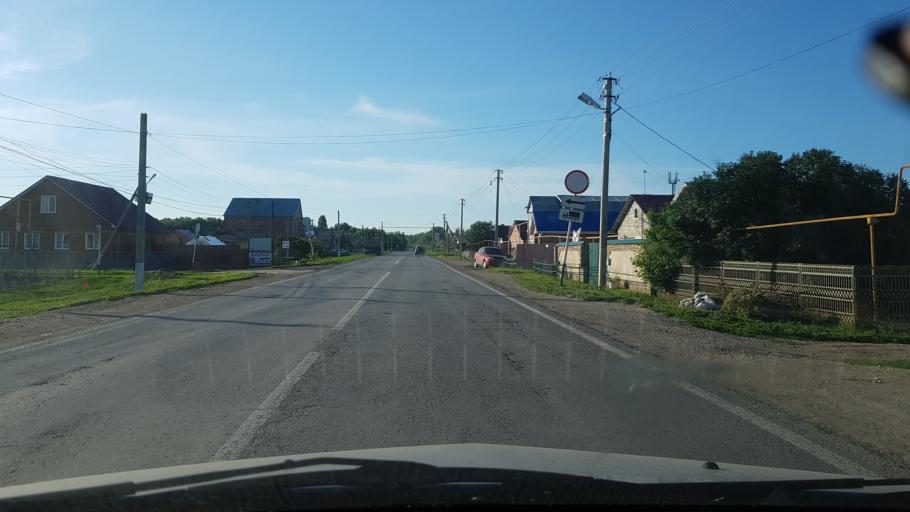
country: RU
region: Samara
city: Tol'yatti
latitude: 53.6483
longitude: 49.2929
